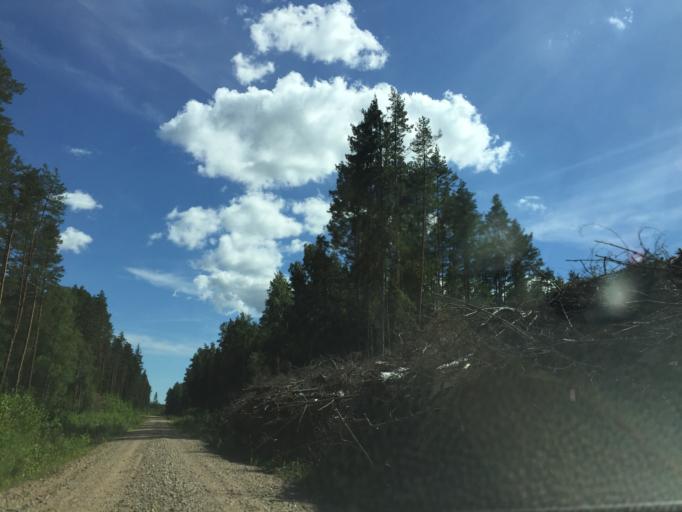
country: LV
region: Ventspils Rajons
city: Piltene
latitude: 57.0972
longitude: 21.8061
